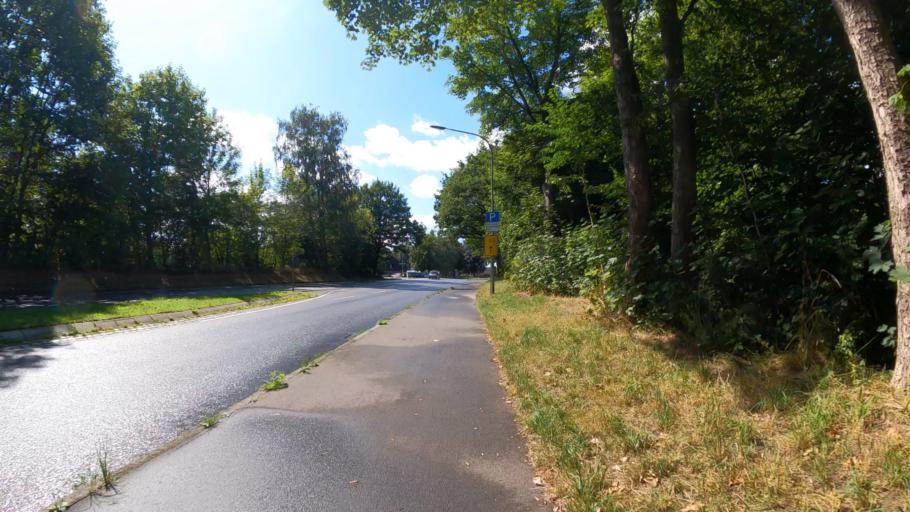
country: DE
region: Schleswig-Holstein
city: Bad Bramstedt
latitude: 53.9285
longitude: 9.8892
